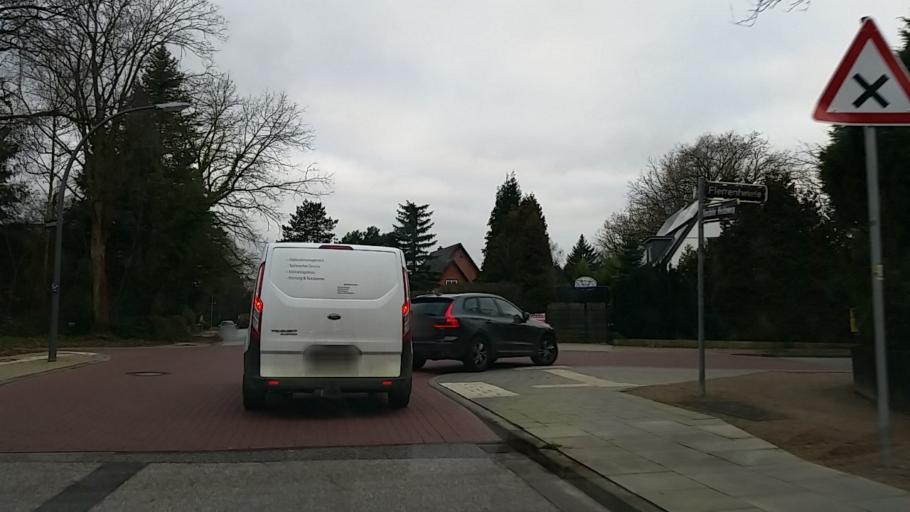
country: DE
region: Schleswig-Holstein
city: Wedel
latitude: 53.5752
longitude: 9.7495
